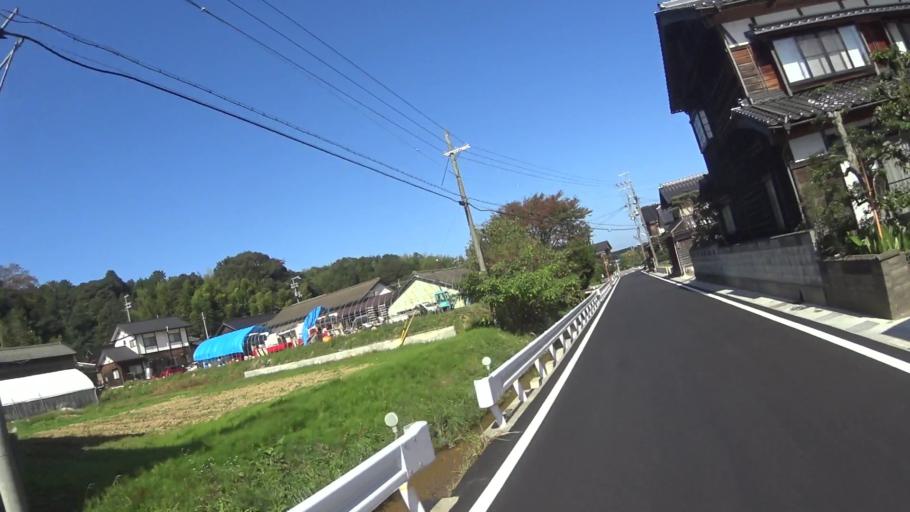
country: JP
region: Kyoto
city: Miyazu
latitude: 35.6790
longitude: 135.0525
